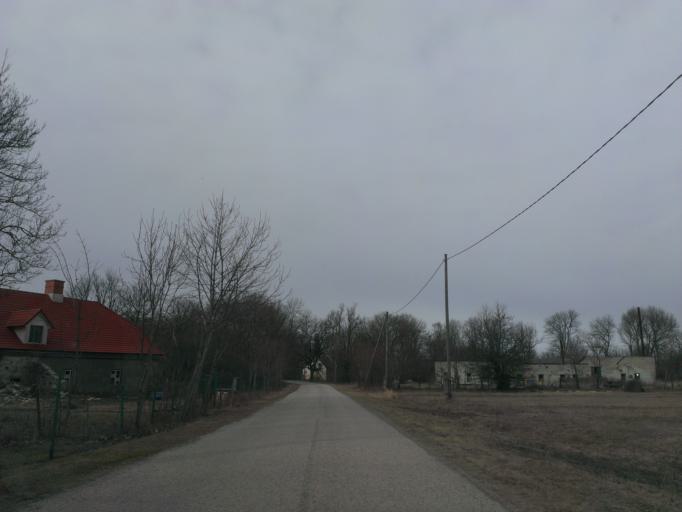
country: EE
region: Laeaene
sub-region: Lihula vald
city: Lihula
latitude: 58.5801
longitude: 23.5402
